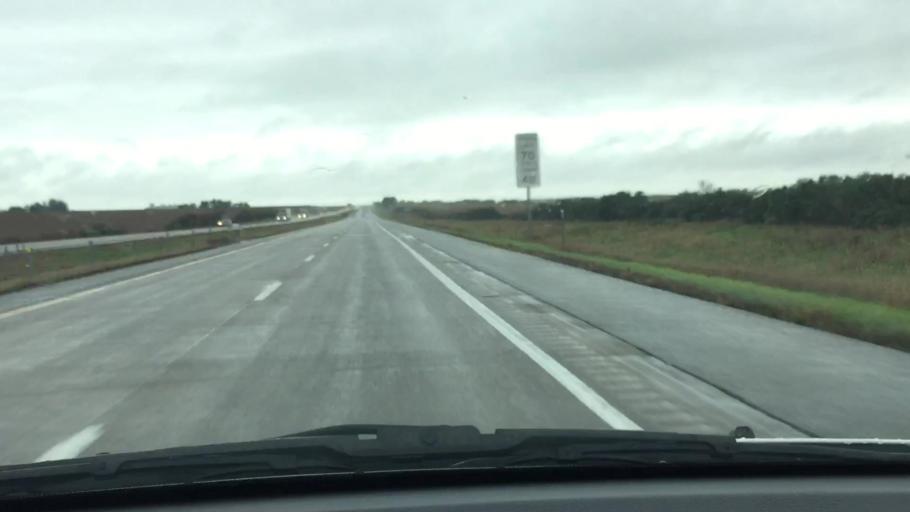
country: US
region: Iowa
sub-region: Poweshiek County
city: Brooklyn
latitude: 41.6955
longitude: -92.4572
